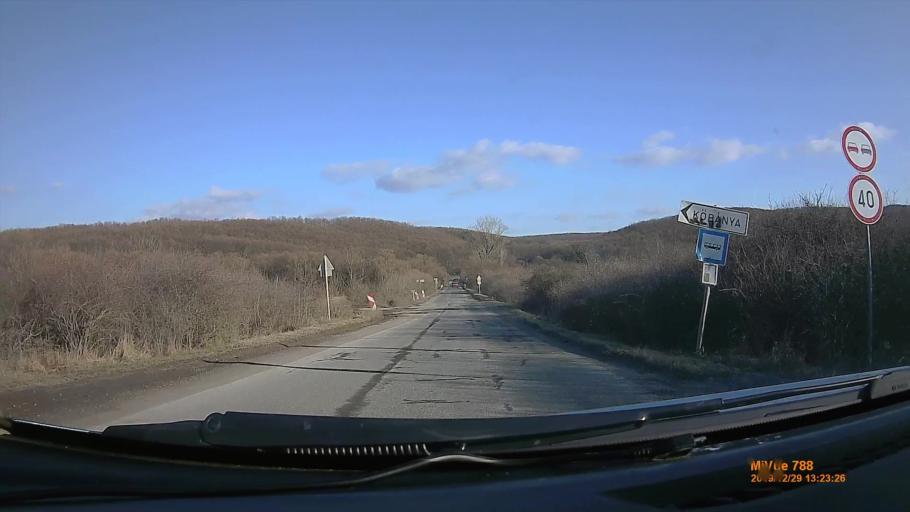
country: HU
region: Heves
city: Domoszlo
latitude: 47.8501
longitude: 20.1713
